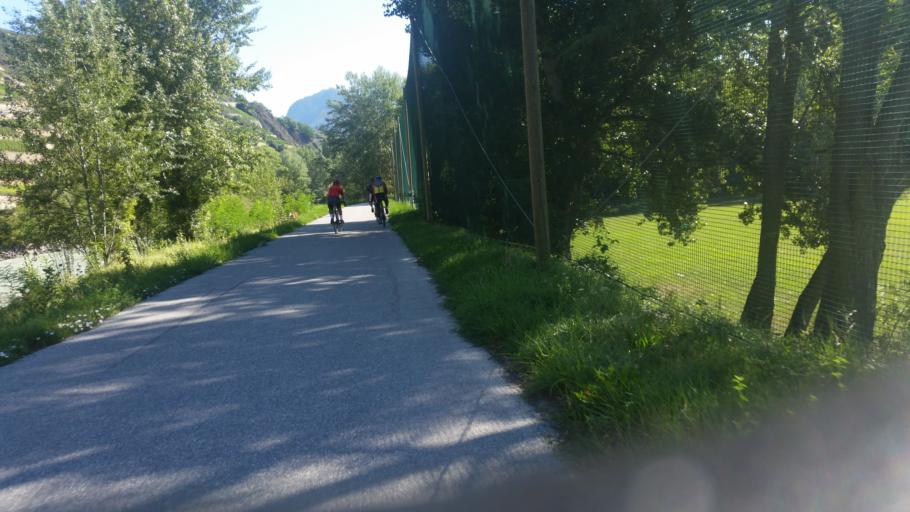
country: CH
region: Valais
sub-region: Sion District
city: Grimisuat
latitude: 46.2431
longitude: 7.3811
